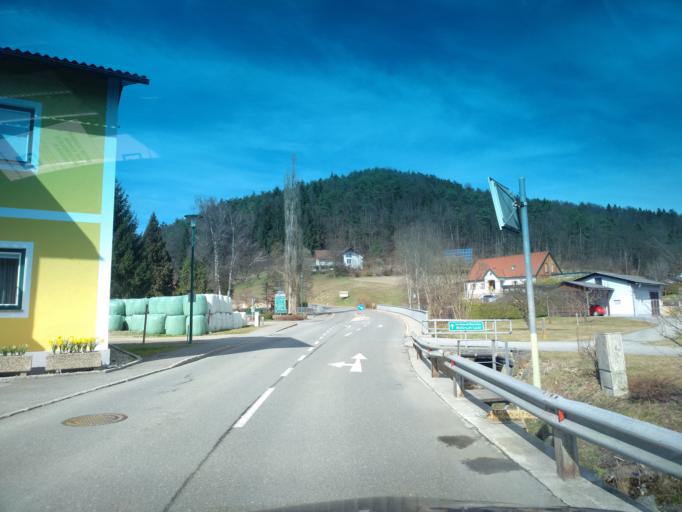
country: AT
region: Styria
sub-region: Politischer Bezirk Leibnitz
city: Kitzeck im Sausal
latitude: 46.7600
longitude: 15.4460
